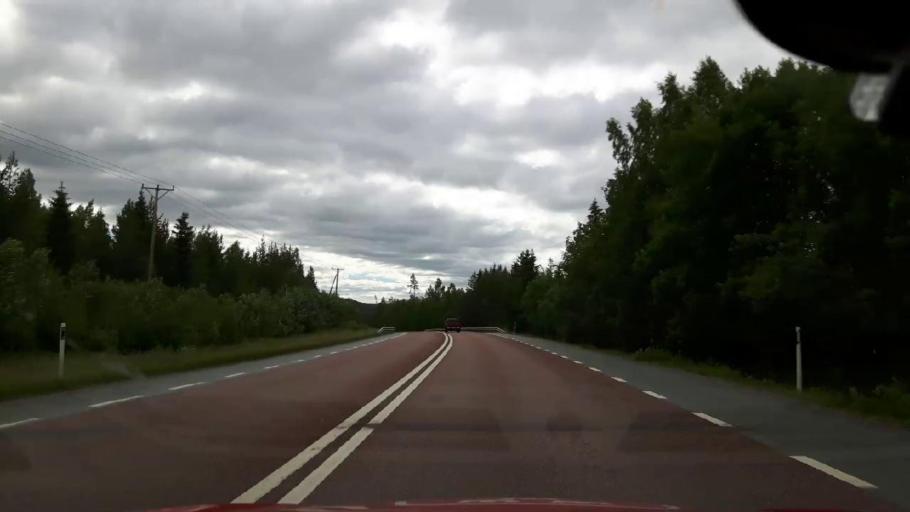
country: SE
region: Jaemtland
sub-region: Braecke Kommun
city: Braecke
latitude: 62.7793
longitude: 15.3872
